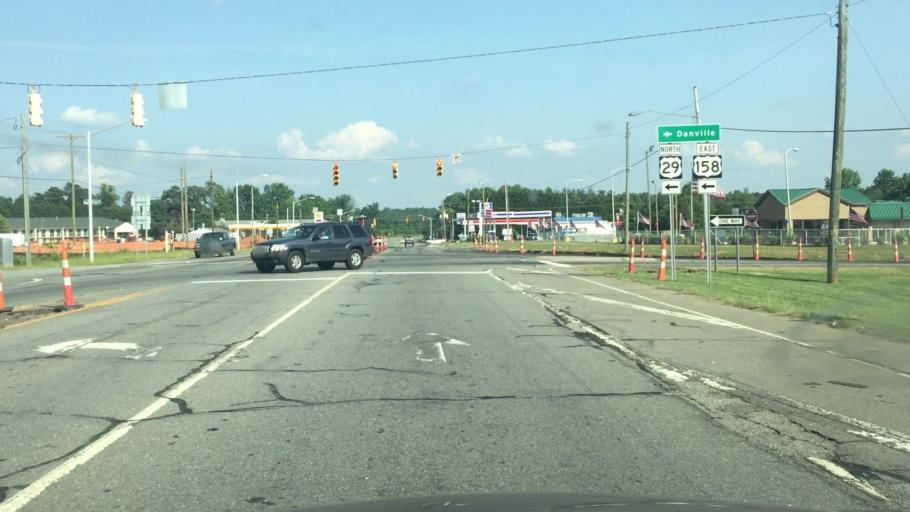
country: US
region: North Carolina
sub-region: Rockingham County
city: Reidsville
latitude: 36.3267
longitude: -79.6425
